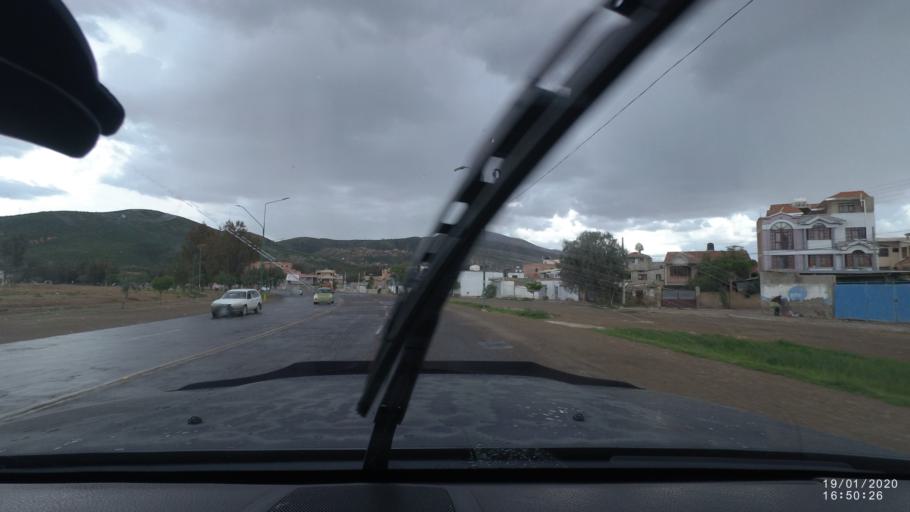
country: BO
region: Cochabamba
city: Cochabamba
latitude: -17.4192
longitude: -66.1350
